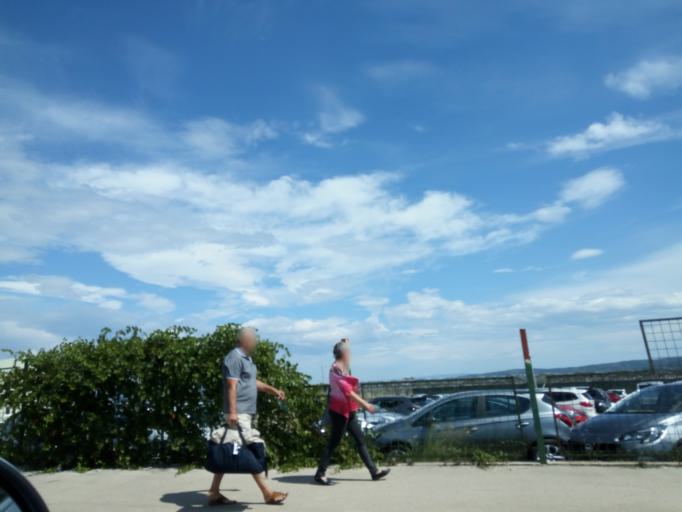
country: HR
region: Splitsko-Dalmatinska
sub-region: Grad Trogir
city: Trogir
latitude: 43.5360
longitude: 16.3011
